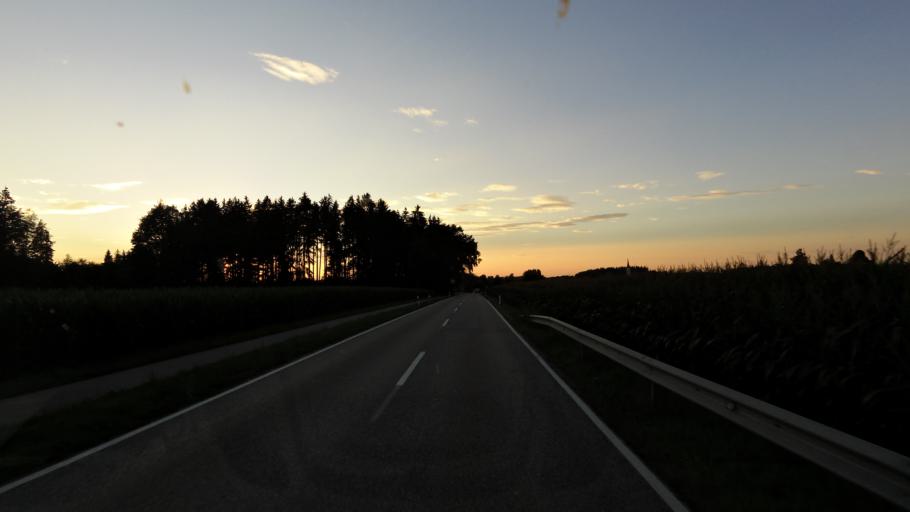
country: DE
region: Bavaria
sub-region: Upper Bavaria
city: Kienberg
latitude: 48.0856
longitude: 12.4782
